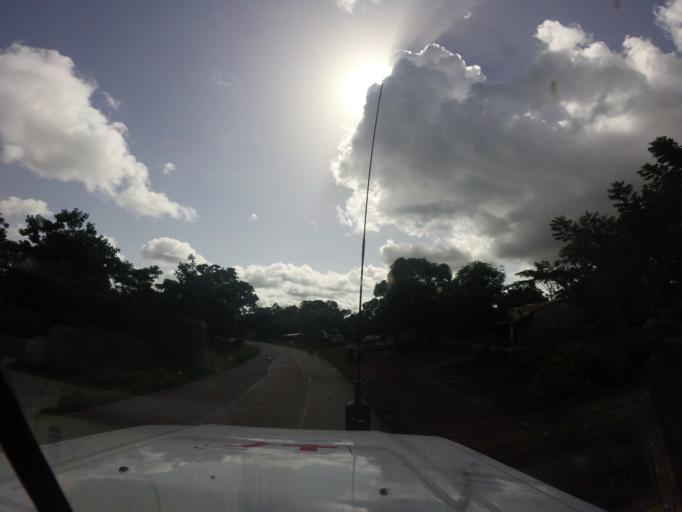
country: GN
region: Mamou
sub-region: Mamou Prefecture
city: Mamou
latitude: 10.3519
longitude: -12.2060
